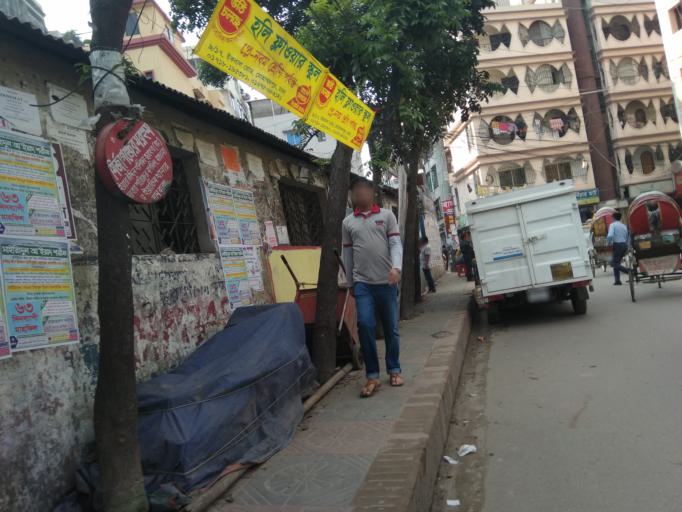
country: BD
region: Dhaka
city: Azimpur
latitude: 23.7660
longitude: 90.3584
